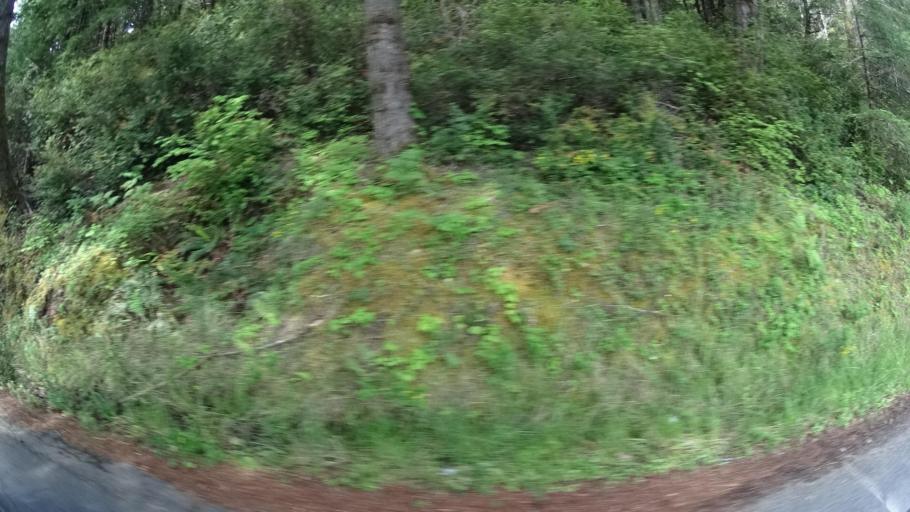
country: US
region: California
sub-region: Humboldt County
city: Redway
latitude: 40.2497
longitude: -123.8329
